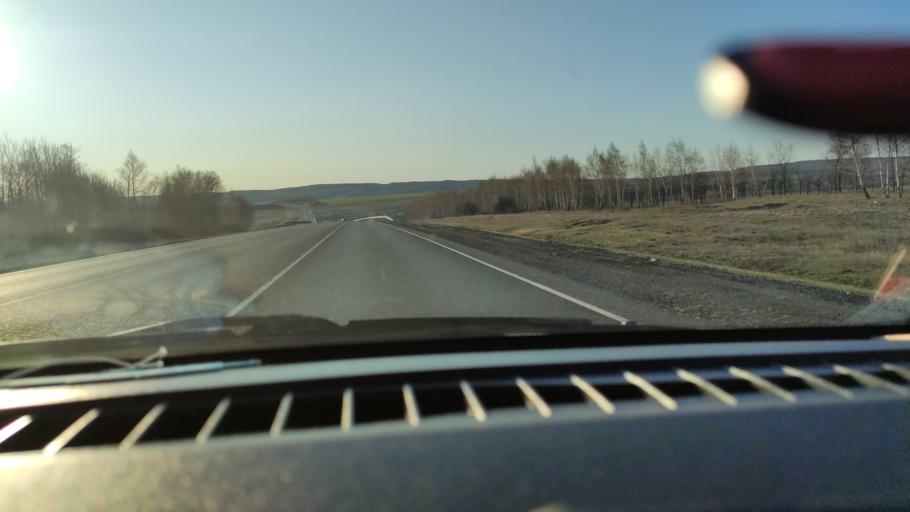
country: RU
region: Saratov
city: Shikhany
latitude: 52.1207
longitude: 47.2633
